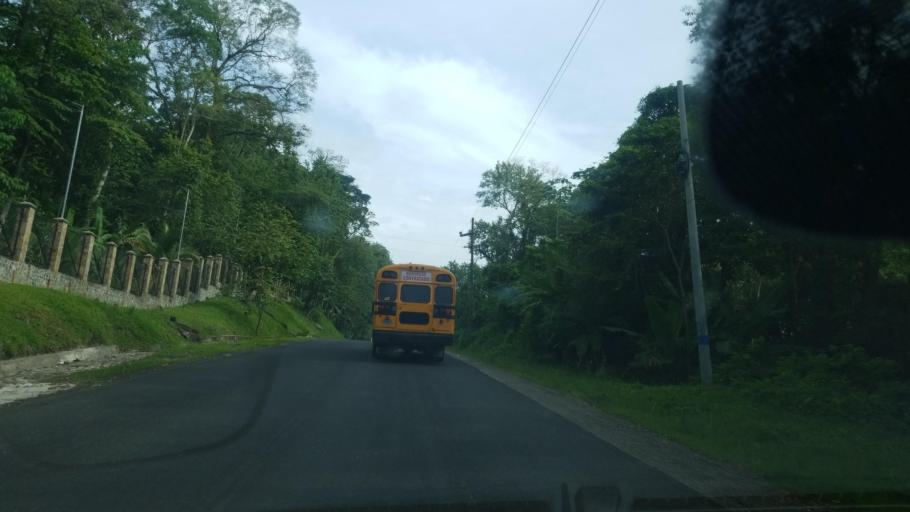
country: HN
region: Santa Barbara
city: Petoa
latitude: 15.2169
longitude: -88.2694
